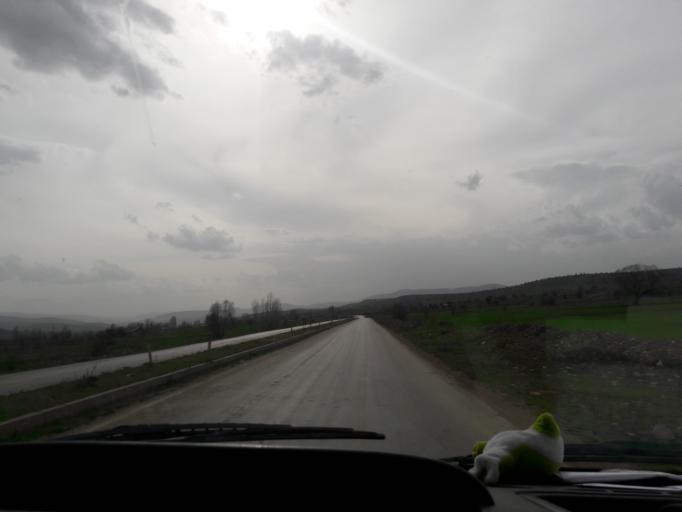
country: TR
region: Gumushane
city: Siran
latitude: 40.1772
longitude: 39.1037
